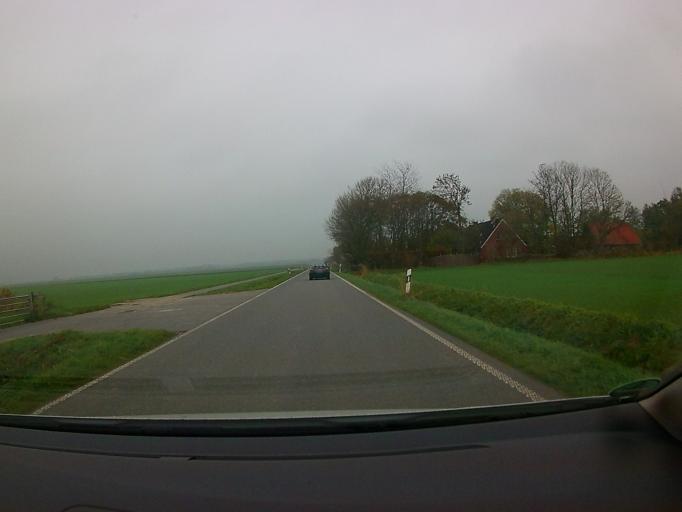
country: DE
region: Schleswig-Holstein
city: Reussenkoge
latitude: 54.6249
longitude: 8.8975
